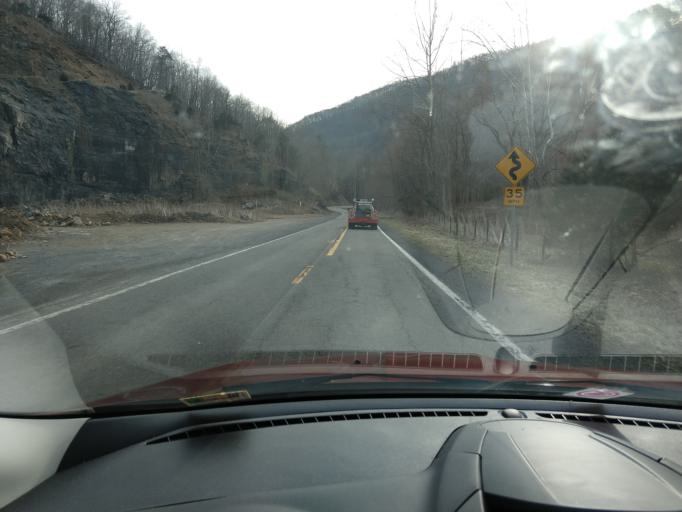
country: US
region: West Virginia
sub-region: Pendleton County
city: Franklin
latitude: 38.5910
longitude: -79.3989
